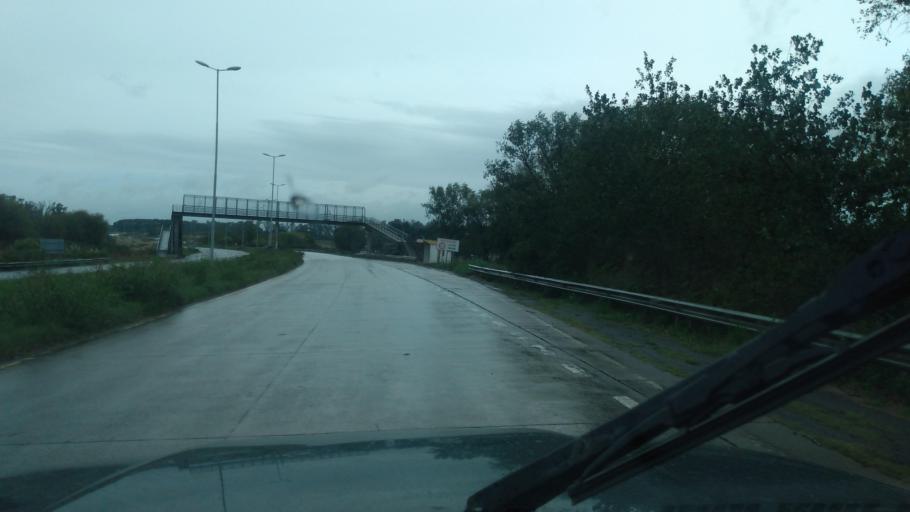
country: AR
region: Buenos Aires
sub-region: Partido de Pilar
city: Pilar
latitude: -34.4014
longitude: -59.0277
